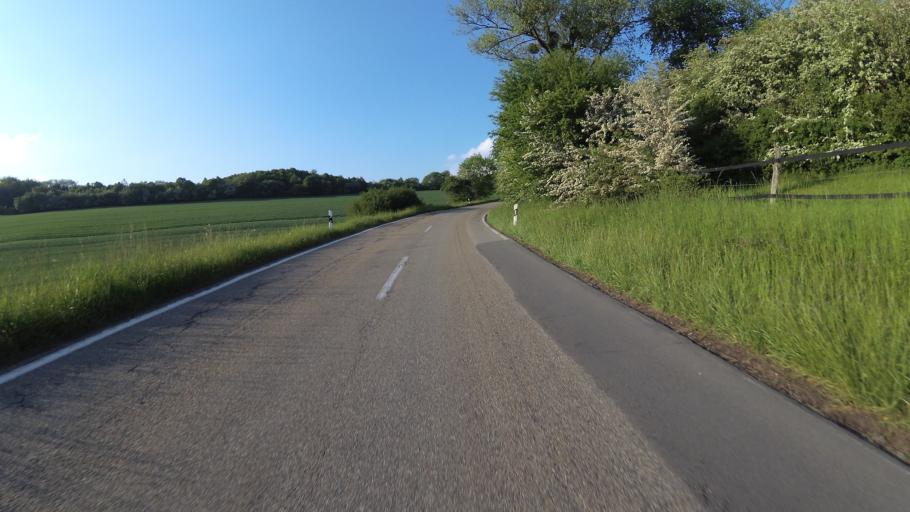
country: DE
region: Rheinland-Pfalz
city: Contwig
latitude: 49.2266
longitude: 7.4132
